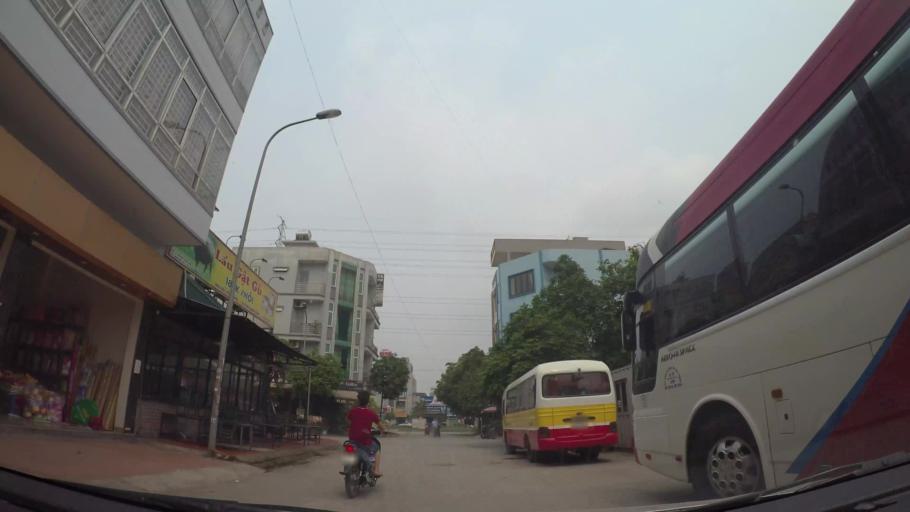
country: VN
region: Ha Noi
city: Ha Dong
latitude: 20.9691
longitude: 105.7549
